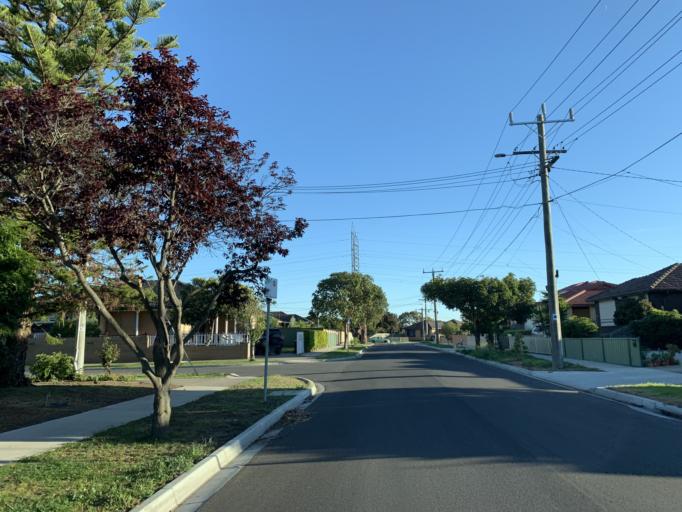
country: AU
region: Victoria
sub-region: Brimbank
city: St Albans
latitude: -37.7532
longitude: 144.8144
